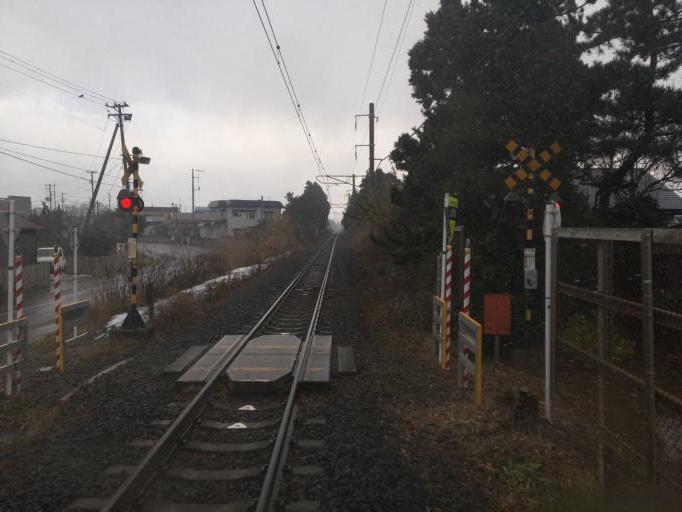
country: JP
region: Aomori
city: Aomori Shi
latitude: 40.9816
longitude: 140.6539
